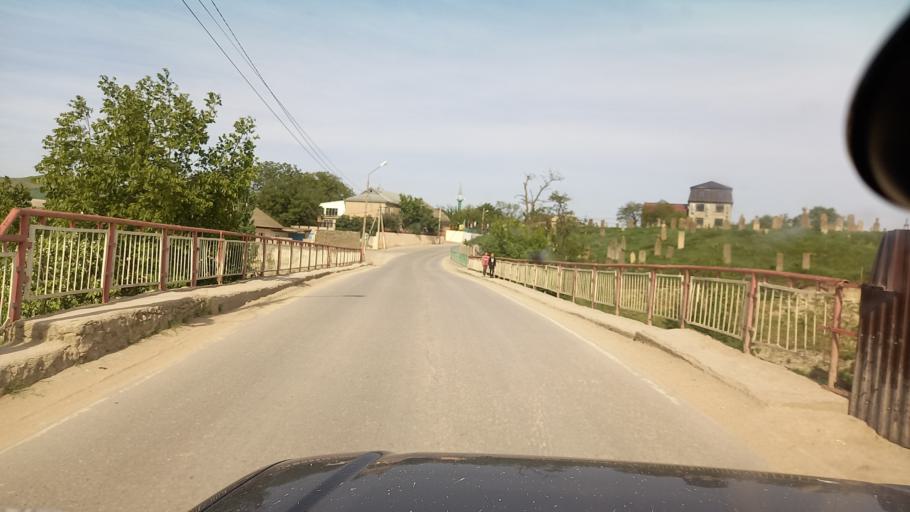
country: RU
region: Dagestan
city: Karabudakhkent
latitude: 42.7084
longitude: 47.5683
